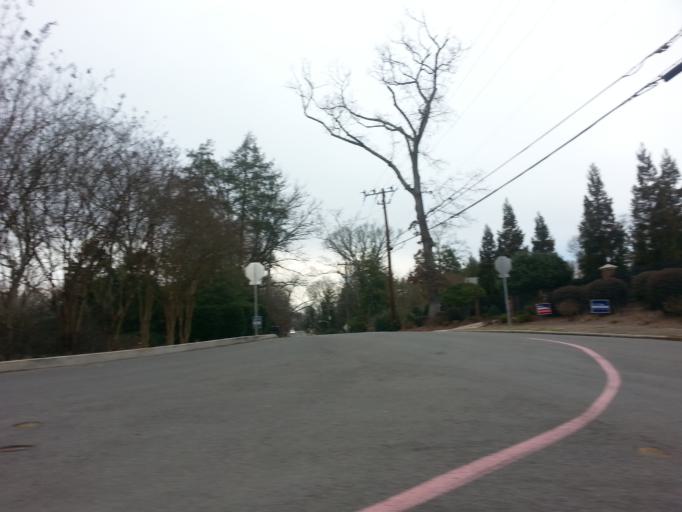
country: US
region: Tennessee
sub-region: Knox County
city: Knoxville
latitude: 35.9371
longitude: -83.9688
